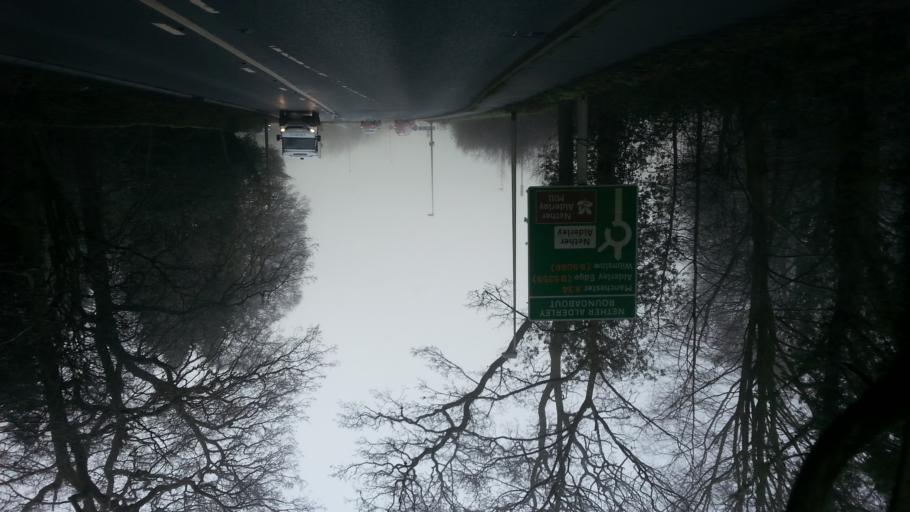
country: GB
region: England
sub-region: Cheshire East
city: Alderley Edge
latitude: 53.2725
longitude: -2.2394
